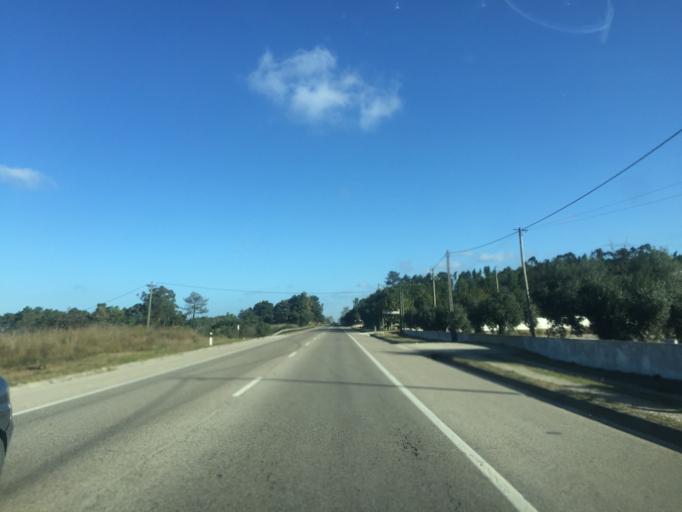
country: PT
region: Leiria
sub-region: Alcobaca
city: Turquel
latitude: 39.4491
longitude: -8.9503
